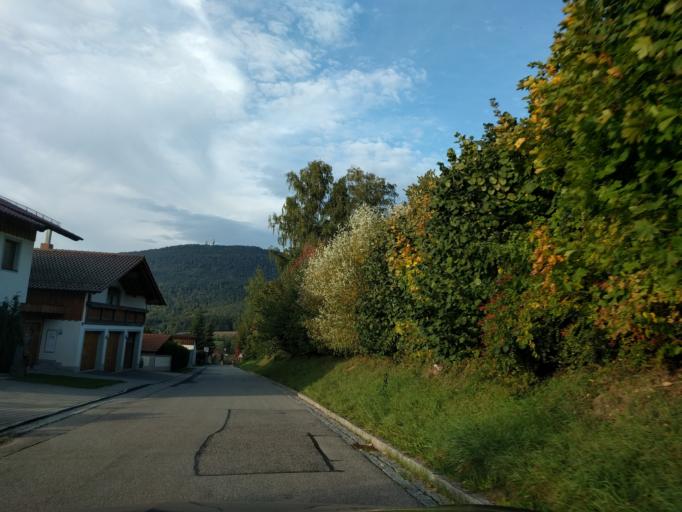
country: DE
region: Bavaria
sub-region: Upper Palatinate
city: Hohenwarth
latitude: 49.2005
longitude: 12.9317
